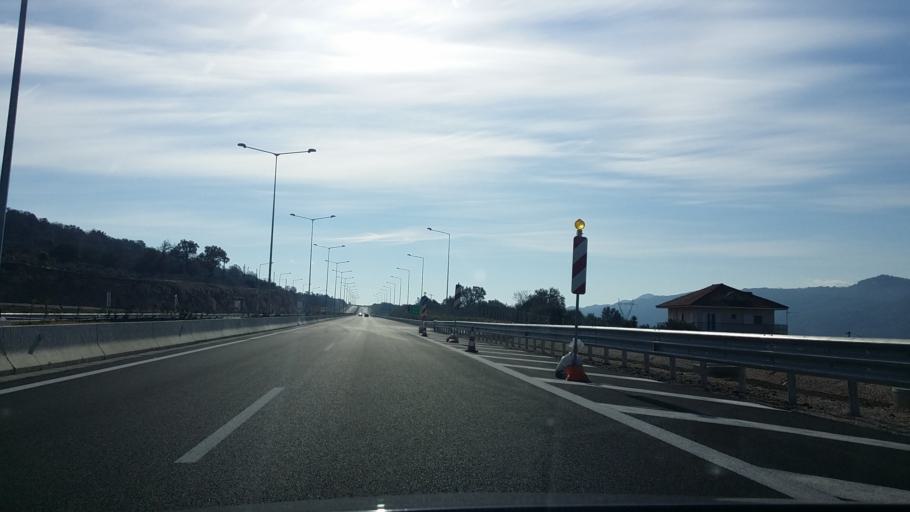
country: GR
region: West Greece
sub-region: Nomos Aitolias kai Akarnanias
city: Fitiai
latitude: 38.7474
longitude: 21.2035
